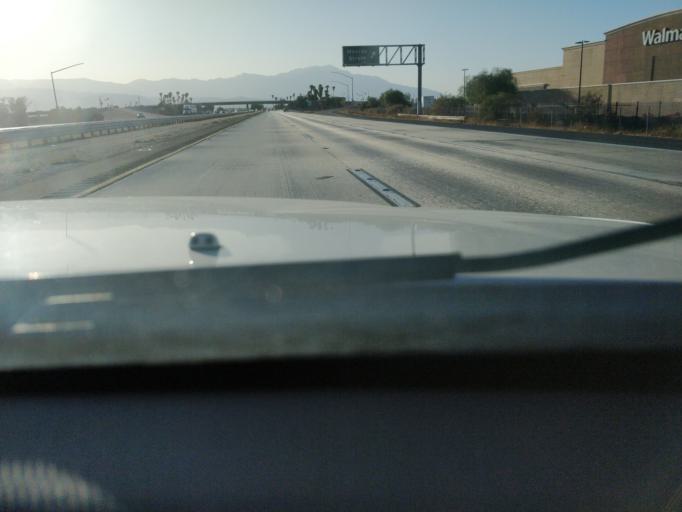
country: US
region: California
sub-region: Riverside County
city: Indio
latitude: 33.7392
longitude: -116.2285
